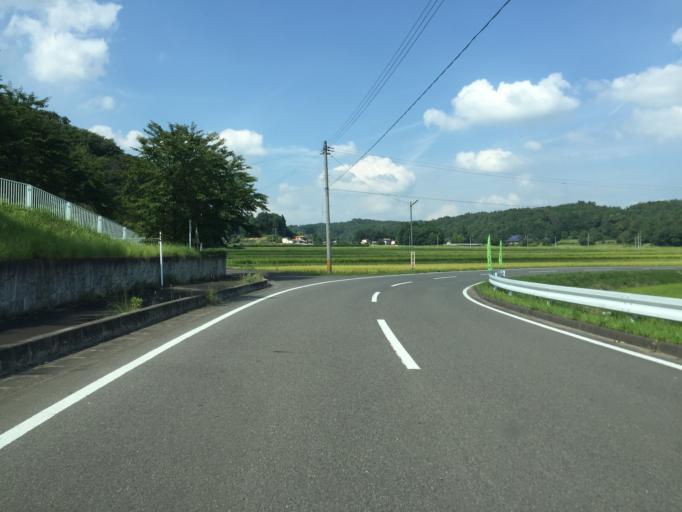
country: JP
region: Fukushima
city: Nihommatsu
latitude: 37.5848
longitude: 140.3856
